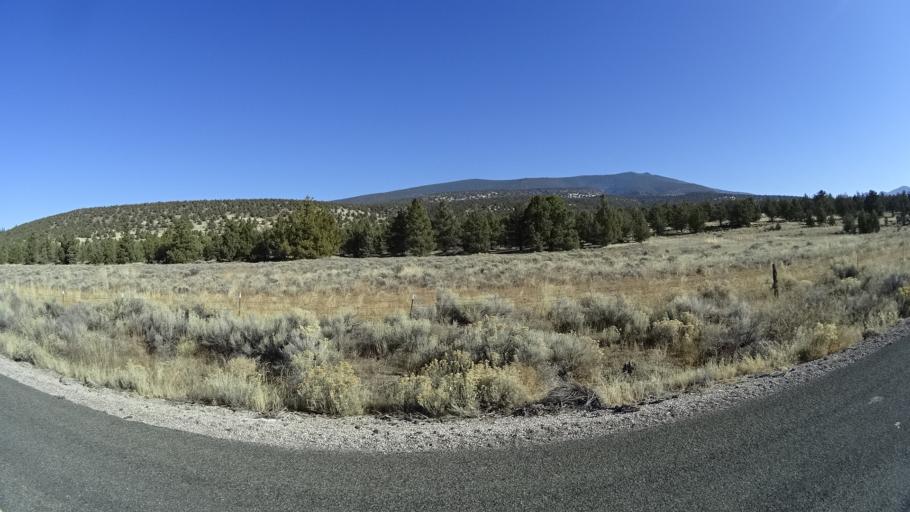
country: US
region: California
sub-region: Siskiyou County
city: Weed
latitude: 41.6152
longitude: -122.3178
